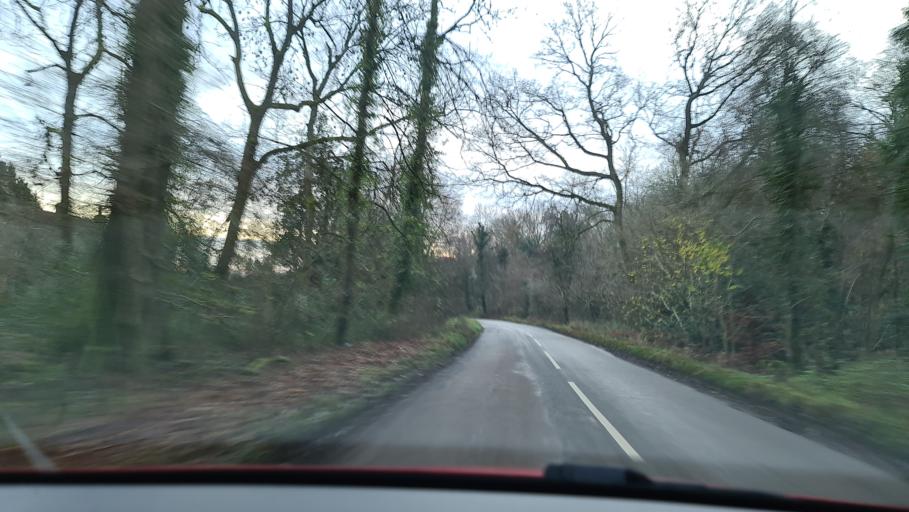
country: GB
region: England
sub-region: Buckinghamshire
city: Princes Risborough
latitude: 51.7089
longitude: -0.7871
